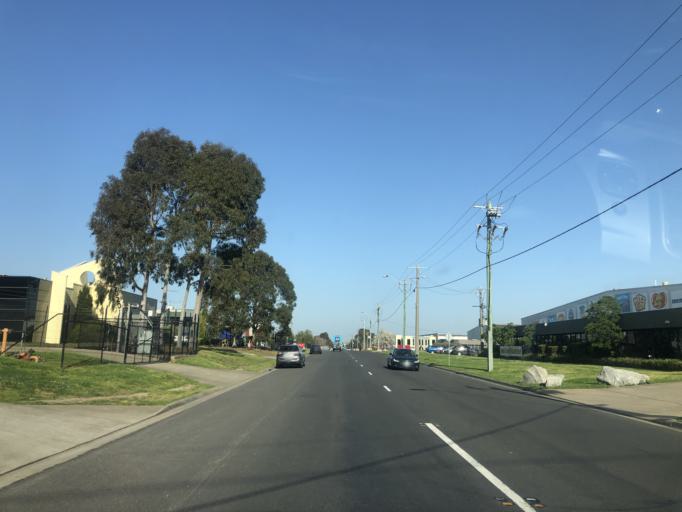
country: AU
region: Victoria
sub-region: Casey
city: Doveton
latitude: -38.0083
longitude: 145.2356
